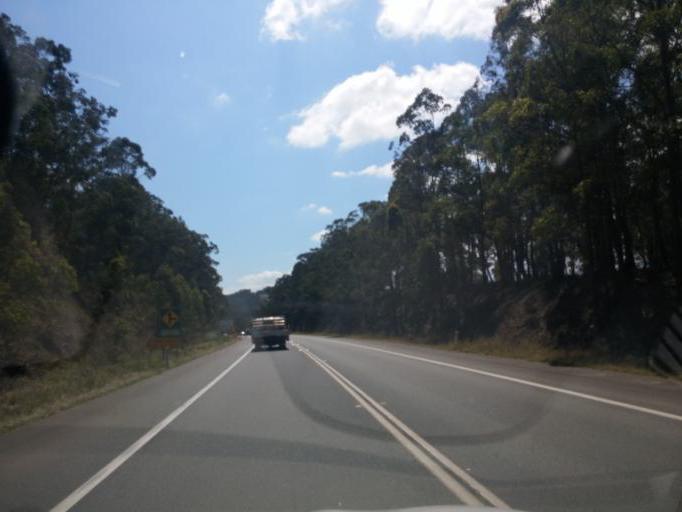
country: AU
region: New South Wales
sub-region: Port Macquarie-Hastings
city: North Shore
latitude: -31.3092
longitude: 152.8190
